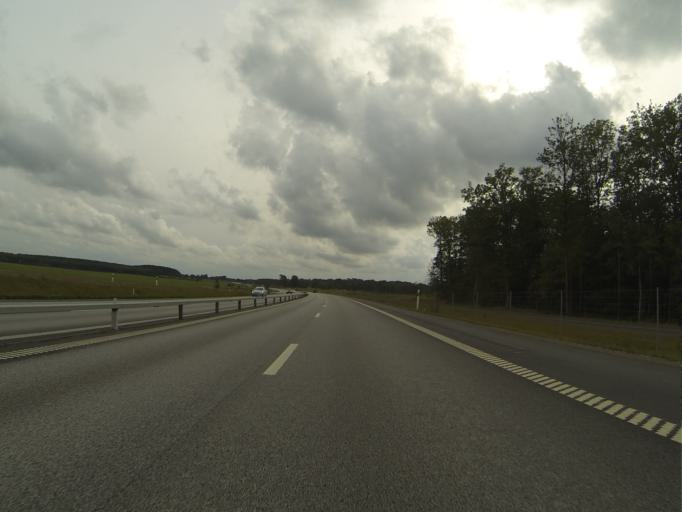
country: SE
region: Skane
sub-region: Horby Kommun
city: Hoerby
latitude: 55.9008
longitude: 13.7278
